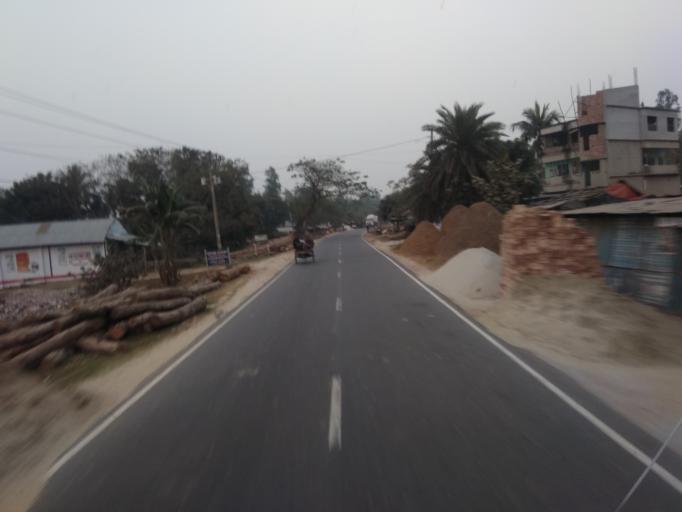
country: BD
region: Rajshahi
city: Bogra
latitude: 24.6492
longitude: 89.2571
